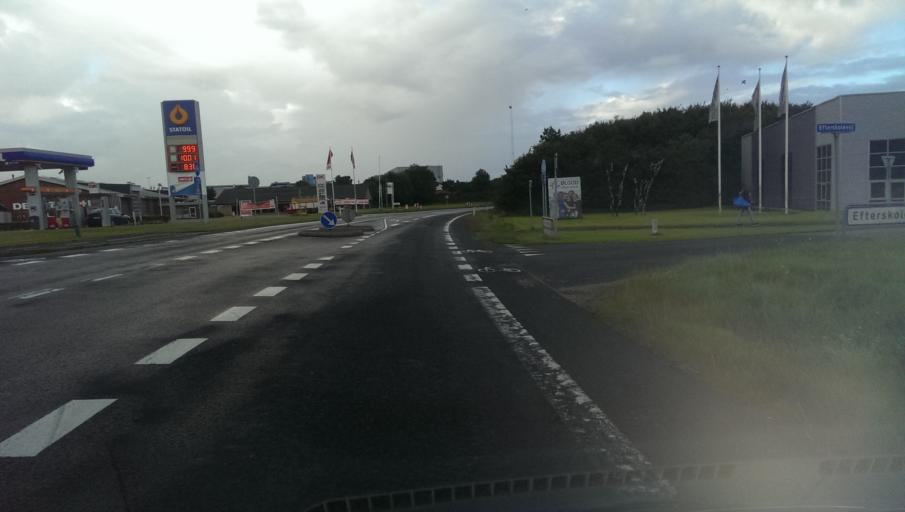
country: DK
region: South Denmark
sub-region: Varde Kommune
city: Olgod
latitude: 55.8074
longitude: 8.6292
